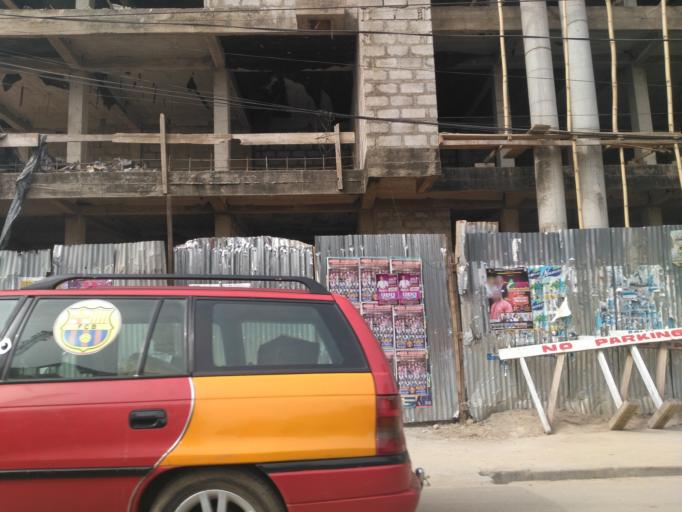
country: GH
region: Ashanti
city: Kumasi
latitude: 6.6913
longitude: -1.6200
